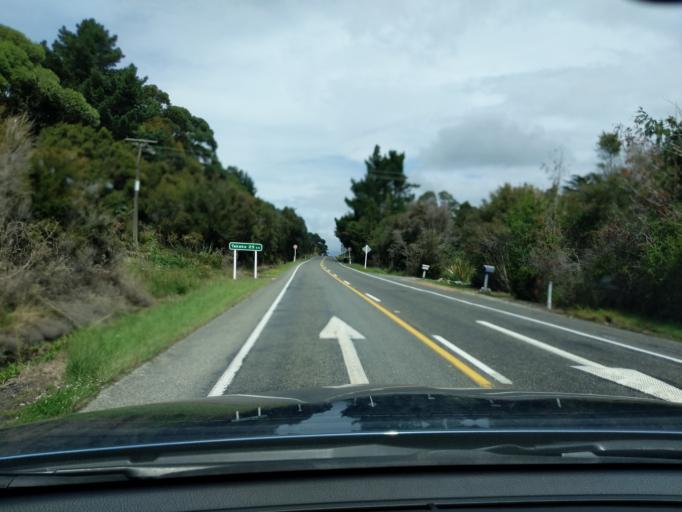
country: NZ
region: Tasman
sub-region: Tasman District
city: Takaka
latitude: -40.6826
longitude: 172.6736
